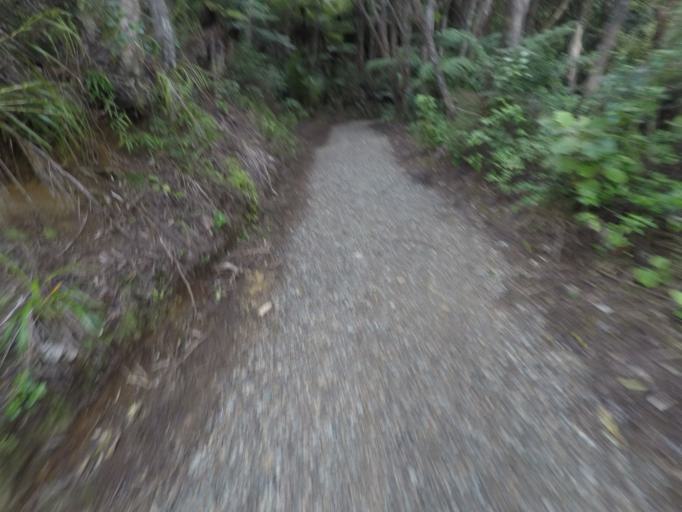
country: NZ
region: Auckland
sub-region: Auckland
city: Muriwai Beach
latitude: -36.9785
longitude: 174.4738
